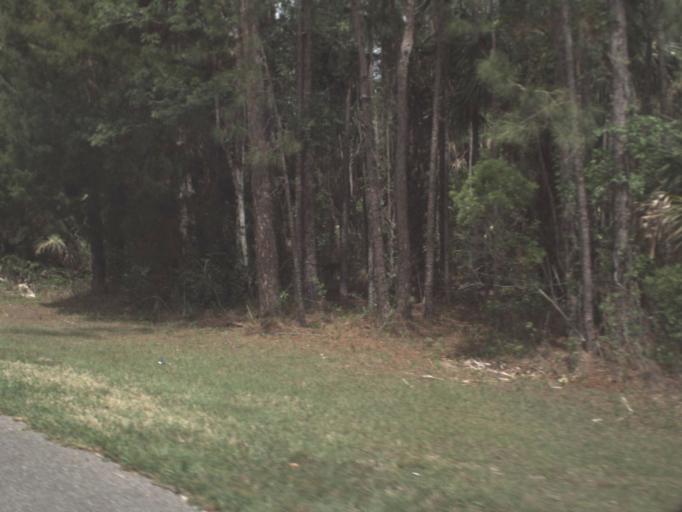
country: US
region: Florida
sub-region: Flagler County
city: Bunnell
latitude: 29.3926
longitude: -81.3082
